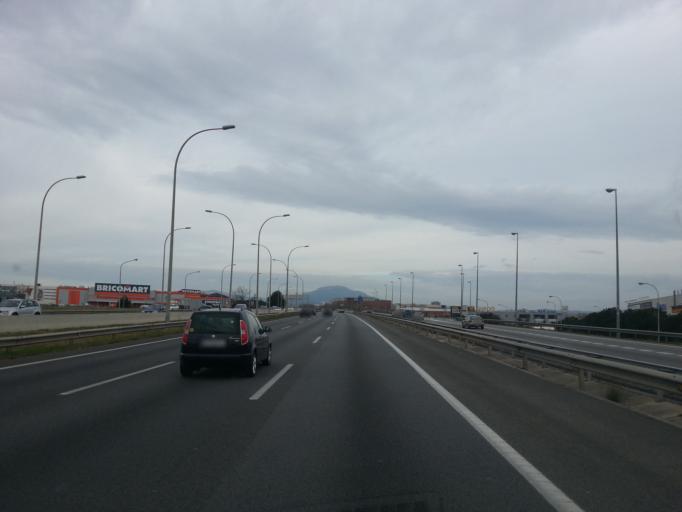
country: ES
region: Catalonia
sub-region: Provincia de Barcelona
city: Sant Quirze del Valles
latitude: 41.5288
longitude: 2.0941
